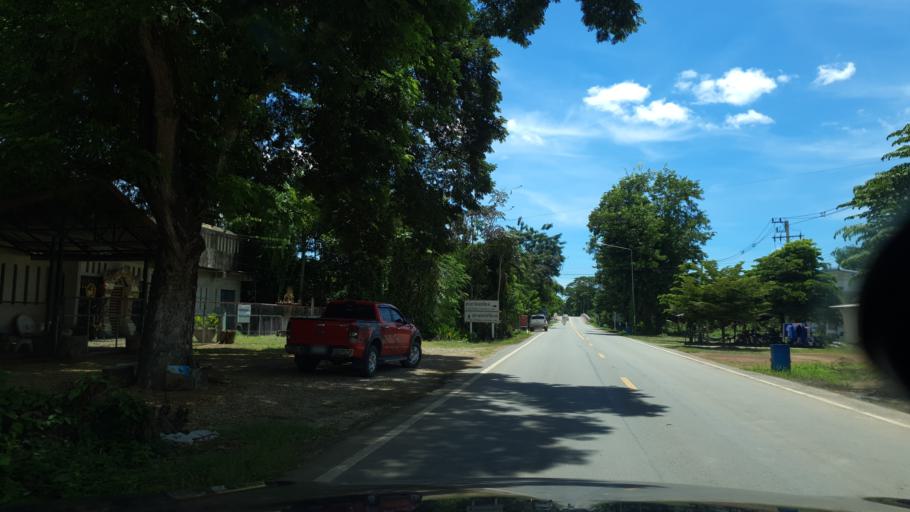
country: TH
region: Sukhothai
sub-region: Amphoe Si Satchanalai
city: Si Satchanalai
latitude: 17.4334
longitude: 99.8016
